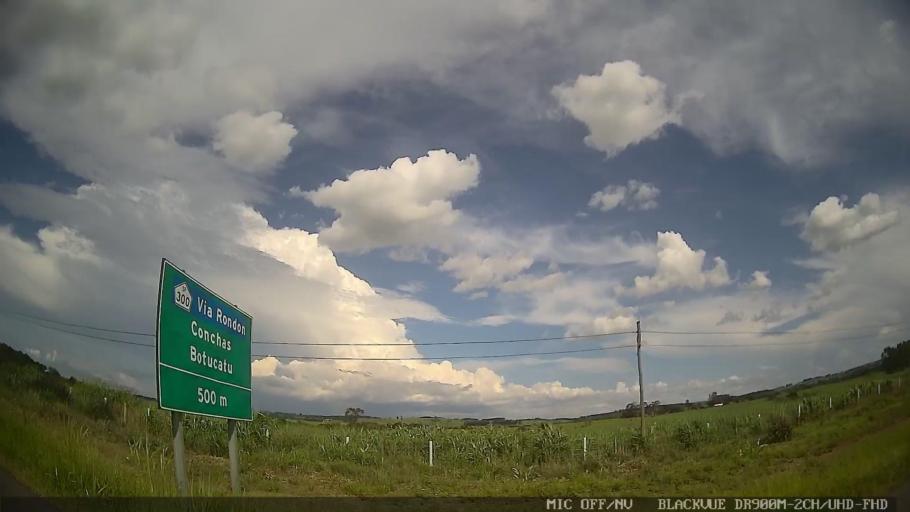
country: BR
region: Sao Paulo
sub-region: Conchas
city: Conchas
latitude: -23.0510
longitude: -47.9585
